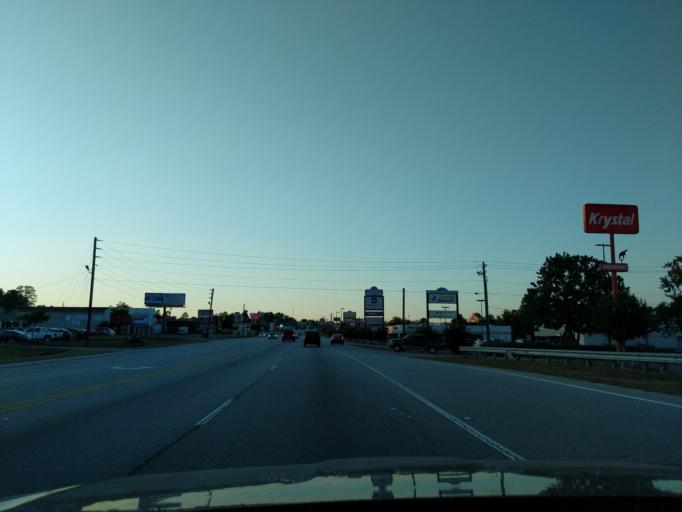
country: US
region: Georgia
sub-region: Columbia County
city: Martinez
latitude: 33.5038
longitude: -82.0890
